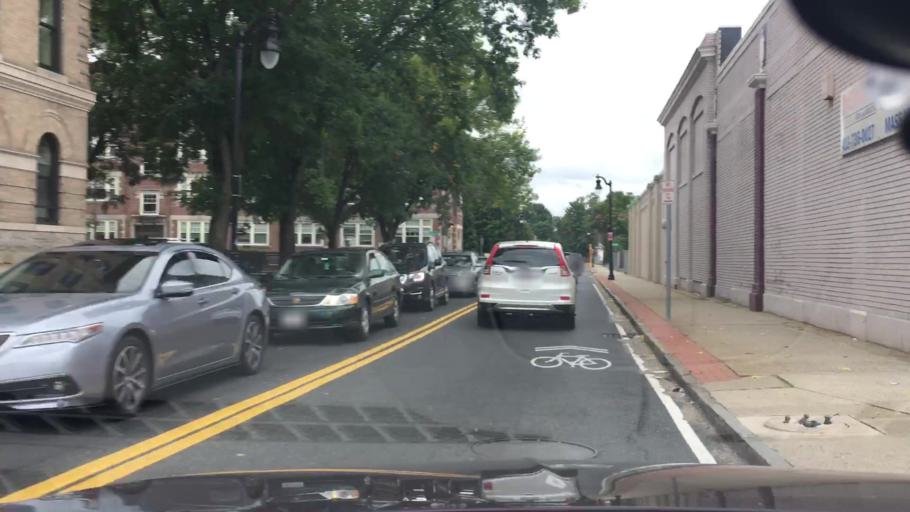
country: US
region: Massachusetts
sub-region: Hampden County
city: Springfield
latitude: 42.1092
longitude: -72.5742
